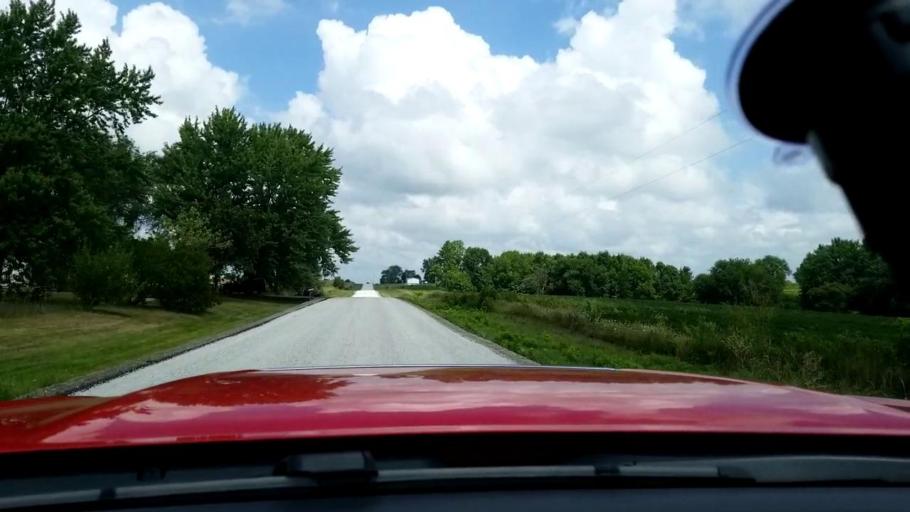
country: US
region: Iowa
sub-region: Decatur County
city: Lamoni
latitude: 40.6333
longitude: -94.0532
